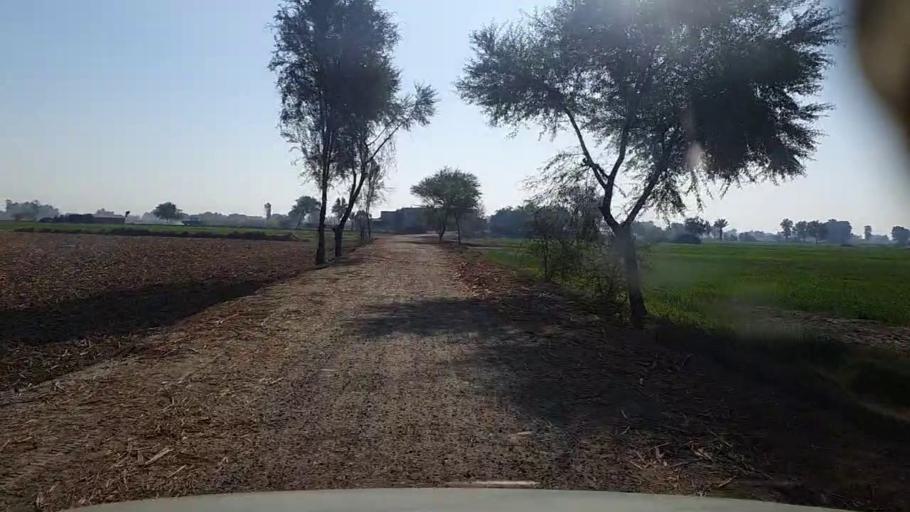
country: PK
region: Sindh
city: Khairpur
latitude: 28.0557
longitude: 69.7378
